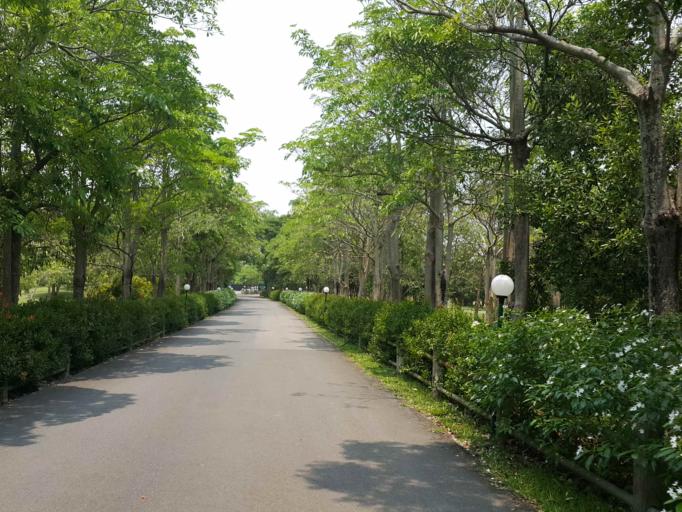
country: TH
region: Chiang Mai
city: San Sai
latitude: 18.9098
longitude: 99.0386
